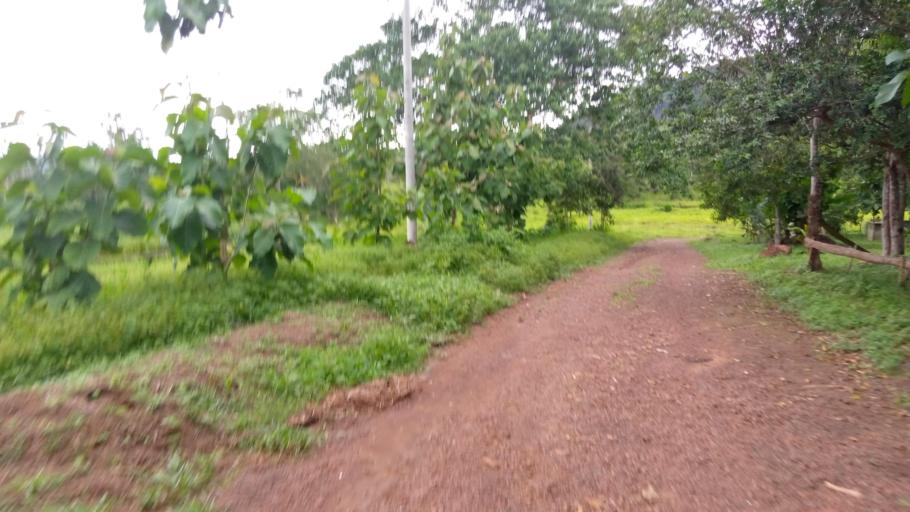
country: SL
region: Southern Province
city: Moyamba
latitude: 8.1582
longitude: -12.4478
